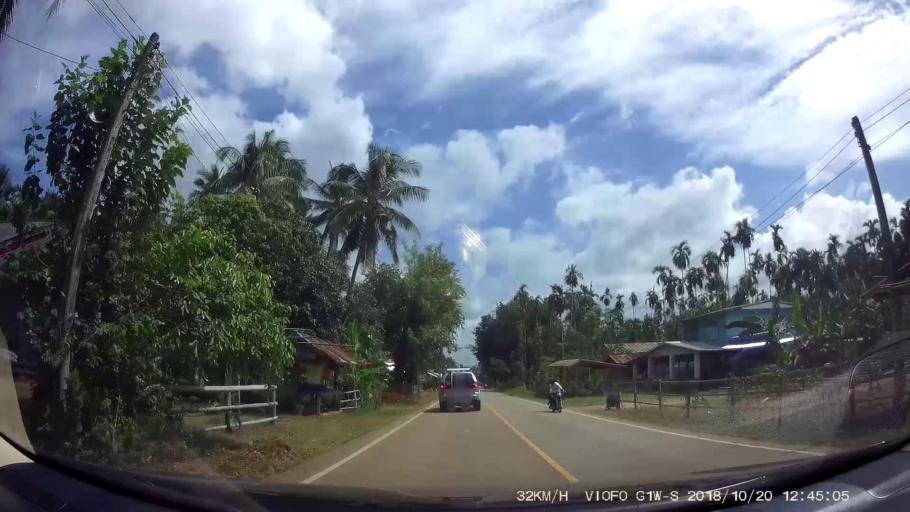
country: TH
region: Chaiyaphum
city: Khon San
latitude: 16.5370
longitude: 101.8729
